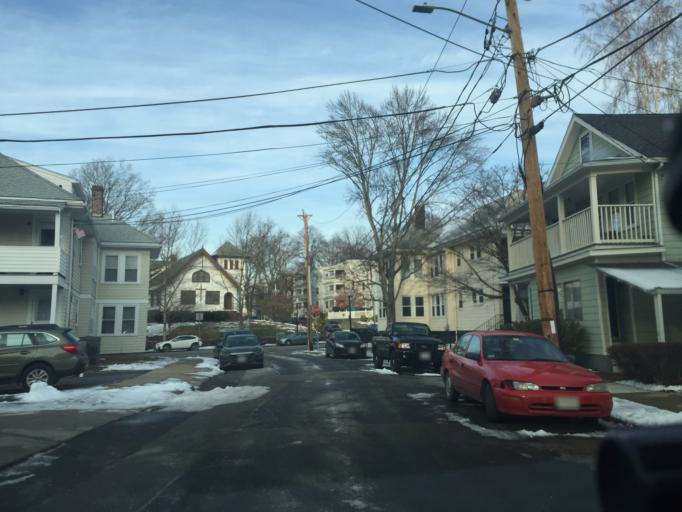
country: US
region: Massachusetts
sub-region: Middlesex County
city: Watertown
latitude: 42.3485
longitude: -71.1626
